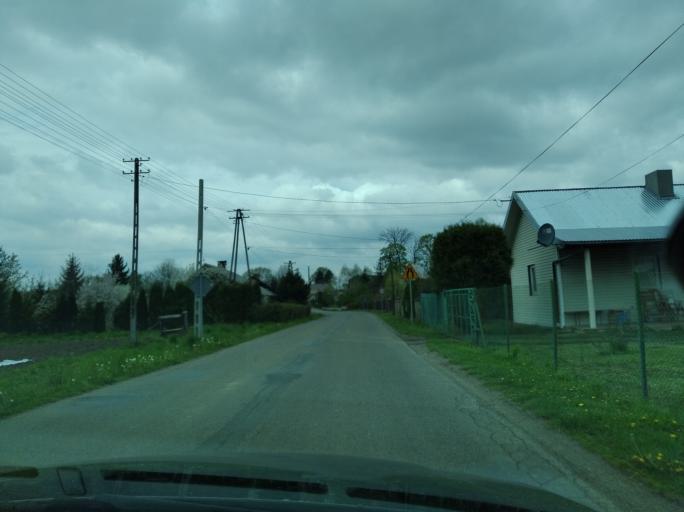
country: PL
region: Subcarpathian Voivodeship
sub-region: Powiat brzozowski
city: Gorki
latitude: 49.6192
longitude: 22.0217
